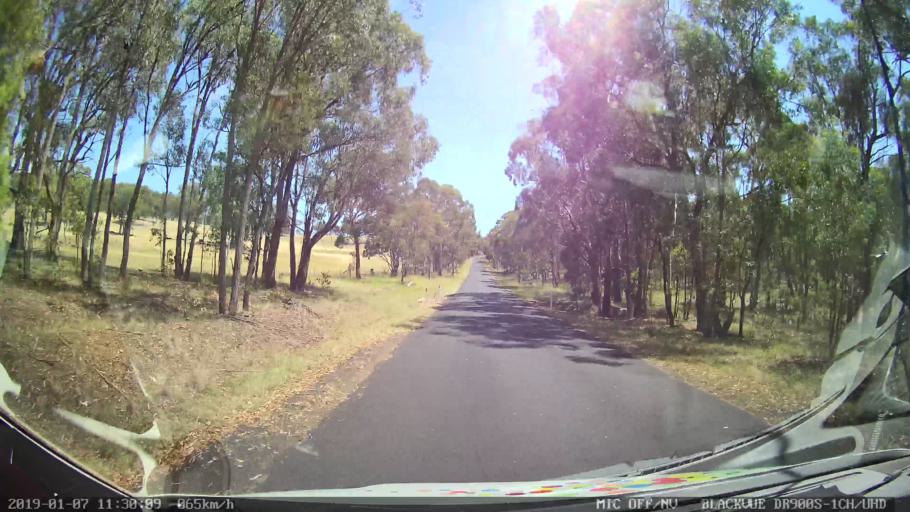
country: AU
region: New South Wales
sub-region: Armidale Dumaresq
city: Armidale
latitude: -30.4319
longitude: 151.5640
